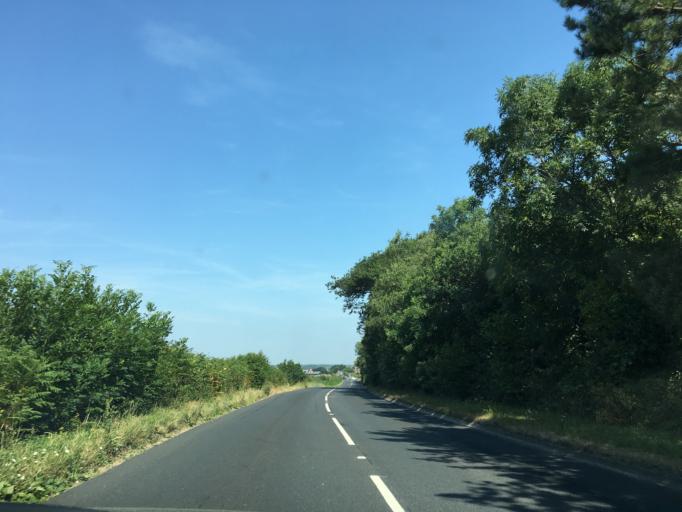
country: GB
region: England
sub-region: Isle of Wight
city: Newchurch
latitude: 50.7013
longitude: -1.2424
